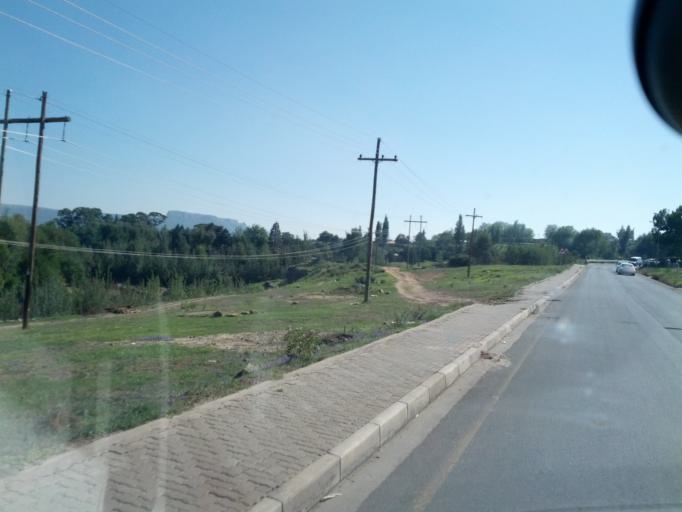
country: LS
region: Maseru
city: Maseru
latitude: -29.3016
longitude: 27.4913
